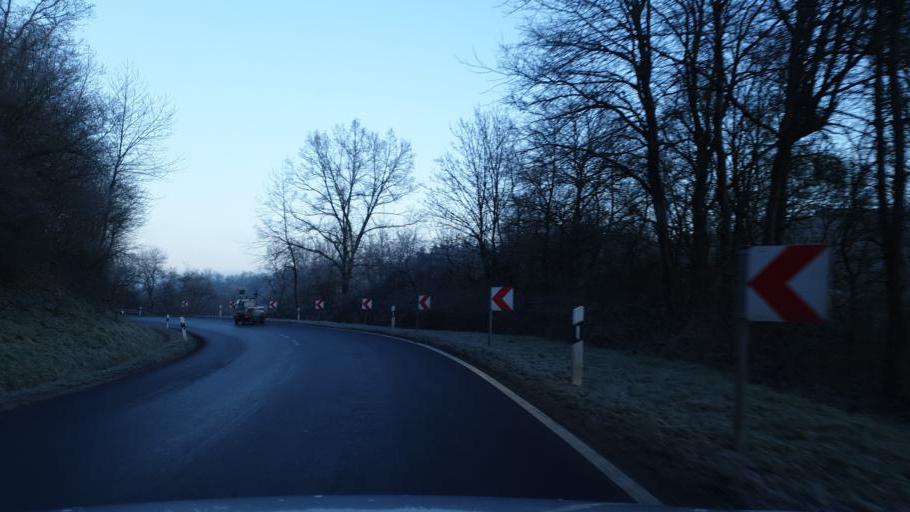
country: DE
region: Hesse
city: Bad Camberg
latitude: 50.2621
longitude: 8.2410
